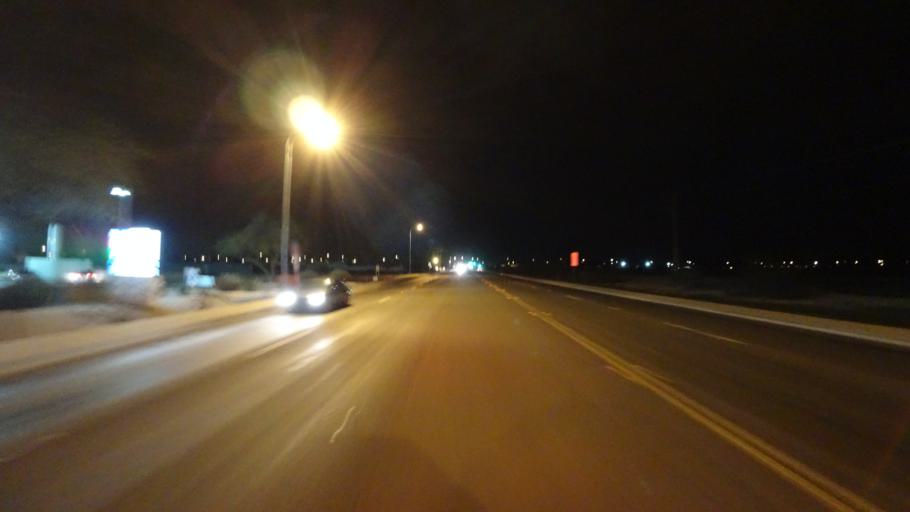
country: US
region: Arizona
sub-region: Pinal County
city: Apache Junction
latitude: 33.3793
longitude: -111.5635
